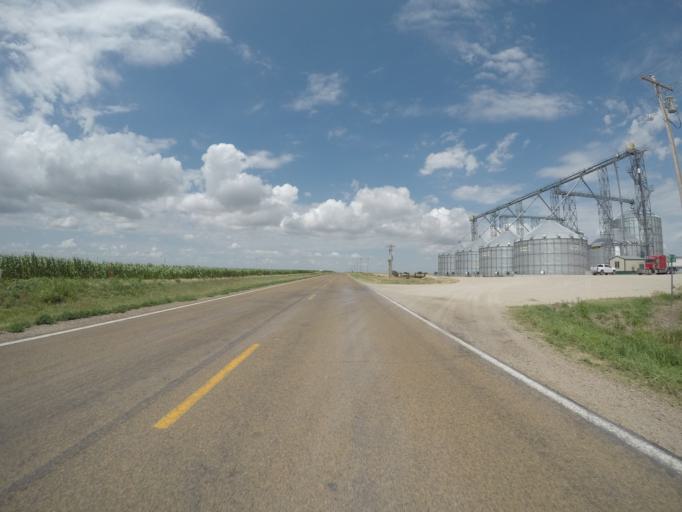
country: US
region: Kansas
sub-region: Rawlins County
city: Atwood
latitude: 39.8716
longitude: -101.0467
